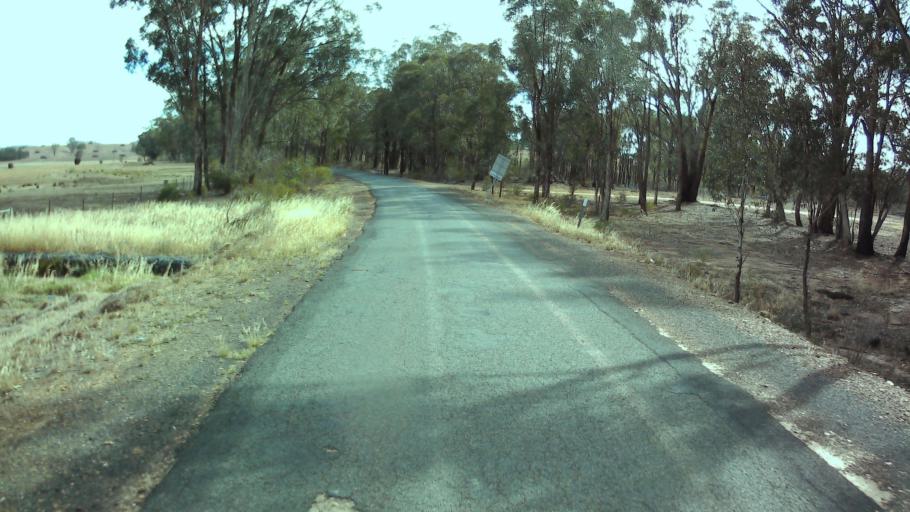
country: AU
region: New South Wales
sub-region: Weddin
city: Grenfell
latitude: -33.8483
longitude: 148.2336
